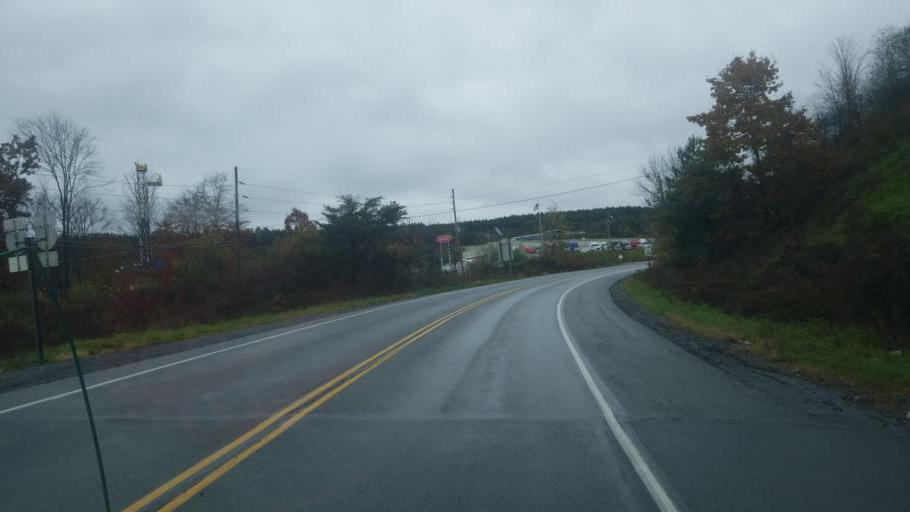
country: US
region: Pennsylvania
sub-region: Clearfield County
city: Clearfield
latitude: 41.0416
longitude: -78.3982
